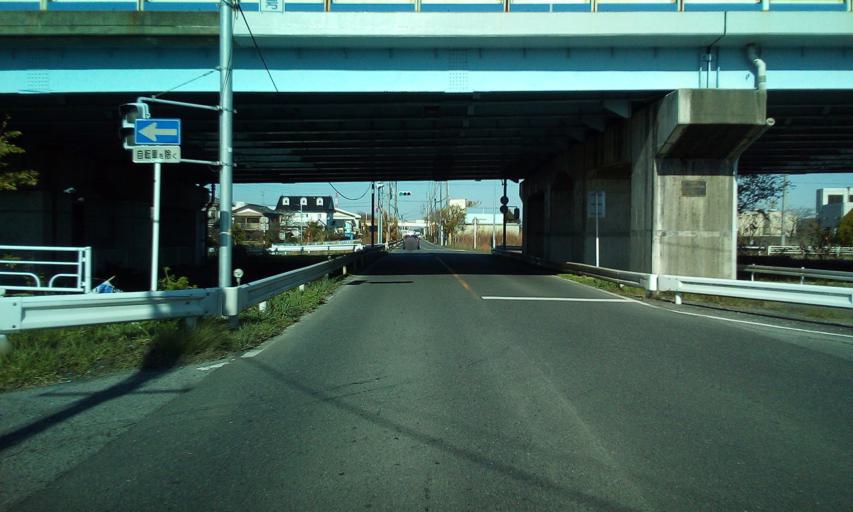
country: JP
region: Saitama
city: Kasukabe
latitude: 35.9895
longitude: 139.7966
